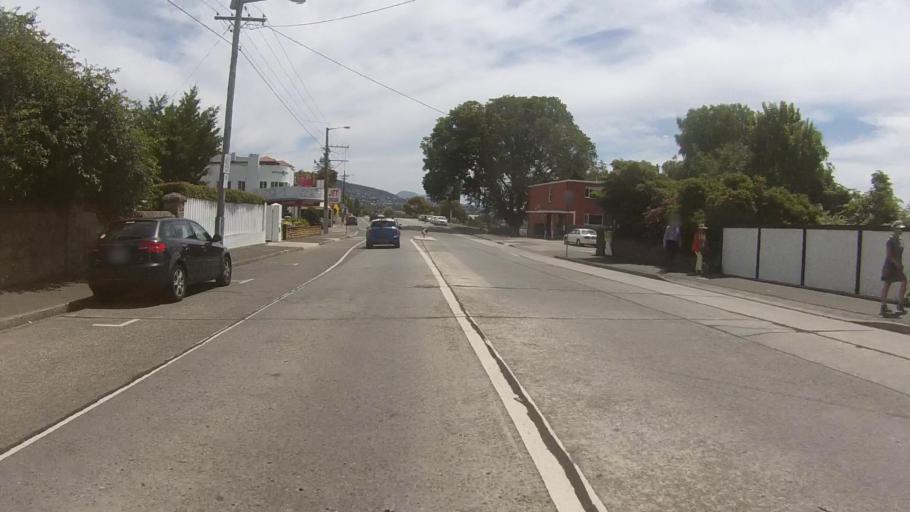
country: AU
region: Tasmania
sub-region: Hobart
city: Sandy Bay
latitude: -42.9075
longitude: 147.3434
